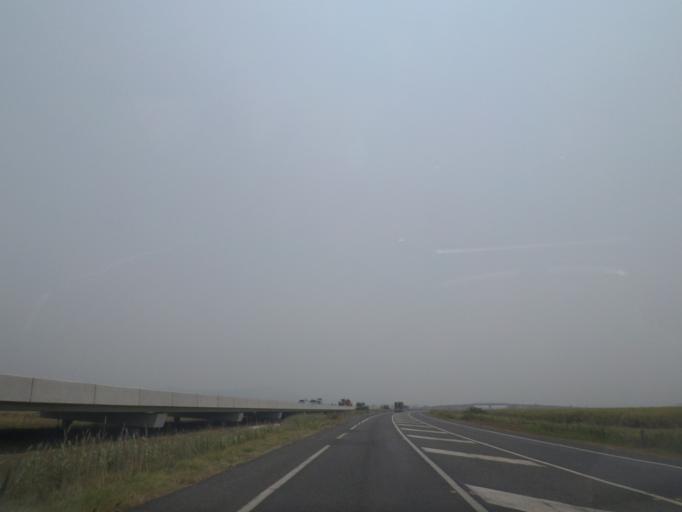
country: AU
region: New South Wales
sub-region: Clarence Valley
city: Maclean
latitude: -29.3994
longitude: 153.2402
